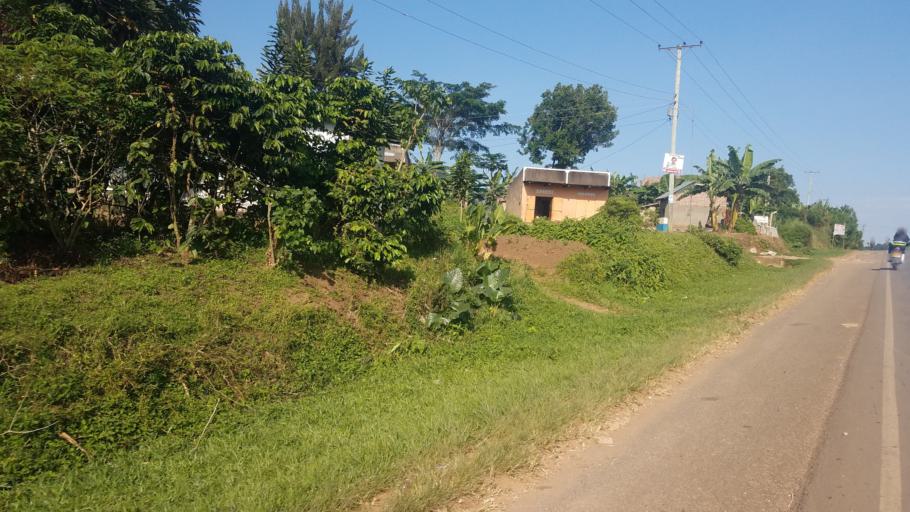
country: UG
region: Central Region
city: Masaka
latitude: -0.3368
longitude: 31.6928
